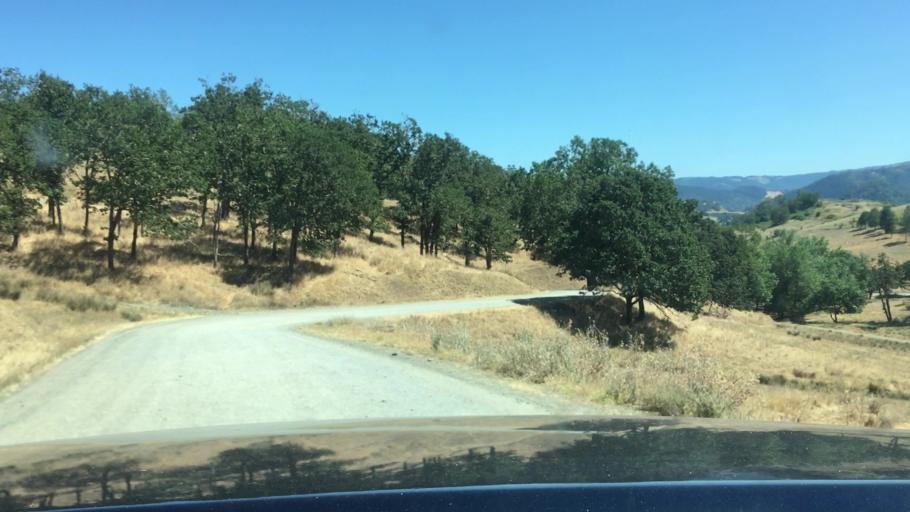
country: US
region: Oregon
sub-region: Douglas County
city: Winston
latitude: 43.1358
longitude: -123.4373
